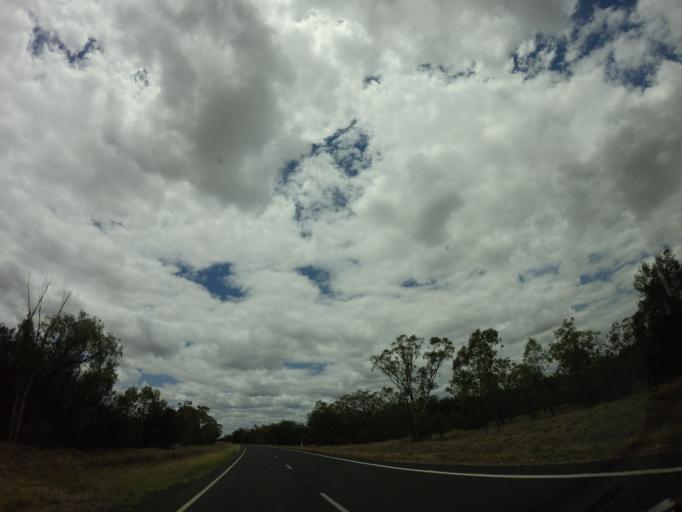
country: AU
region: Queensland
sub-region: Goondiwindi
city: Goondiwindi
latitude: -28.1727
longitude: 150.5713
